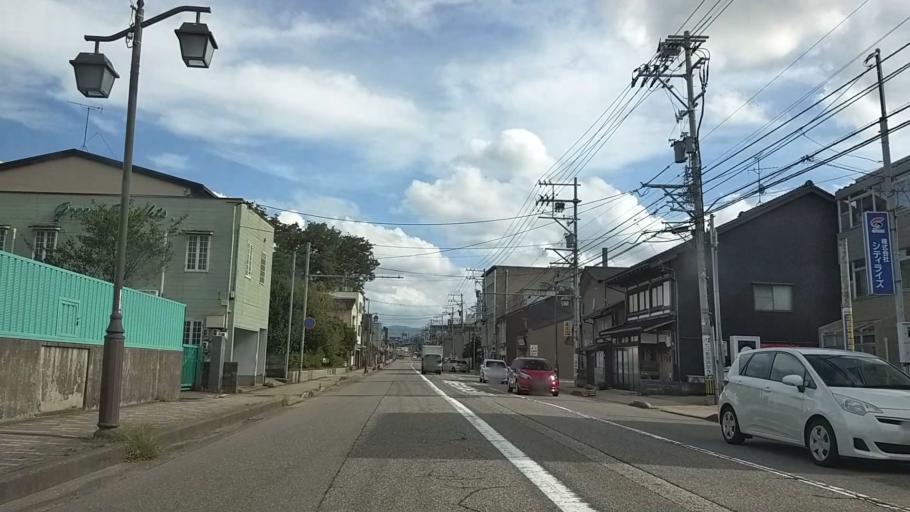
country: JP
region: Ishikawa
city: Nonoichi
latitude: 36.5455
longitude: 136.6600
